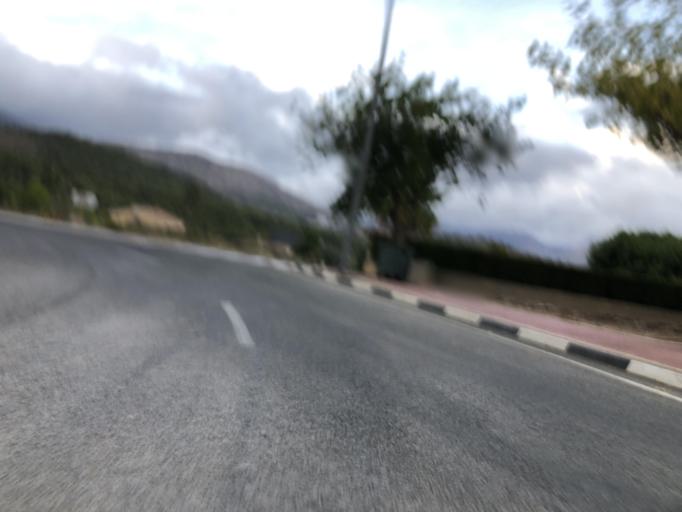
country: ES
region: Valencia
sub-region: Provincia de Alicante
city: Polop
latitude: 38.6302
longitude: -0.1477
